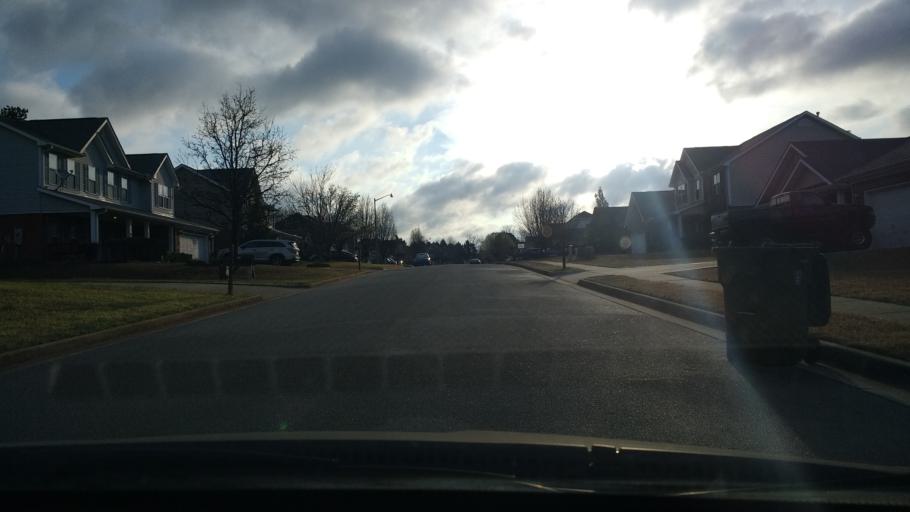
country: US
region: Alabama
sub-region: Madison County
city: Madison
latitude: 34.7138
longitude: -86.7495
